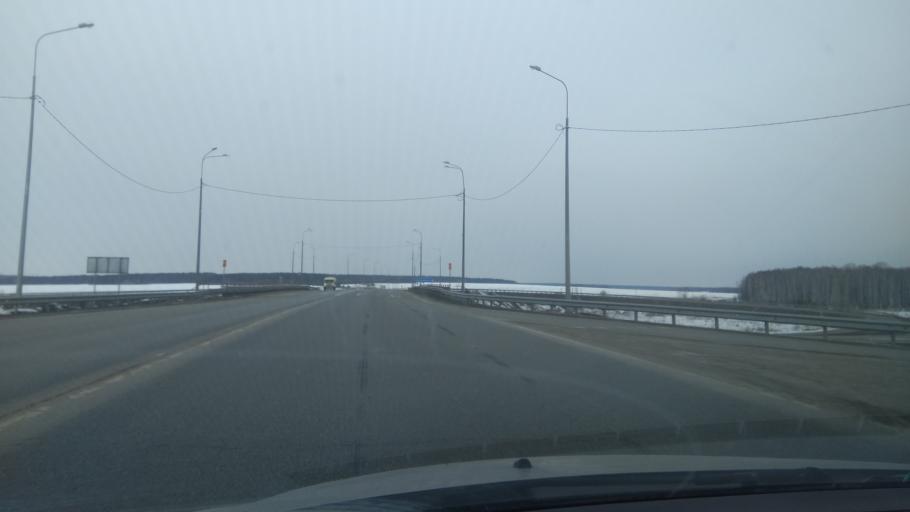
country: RU
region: Sverdlovsk
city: Achit
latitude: 56.7885
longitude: 57.8829
